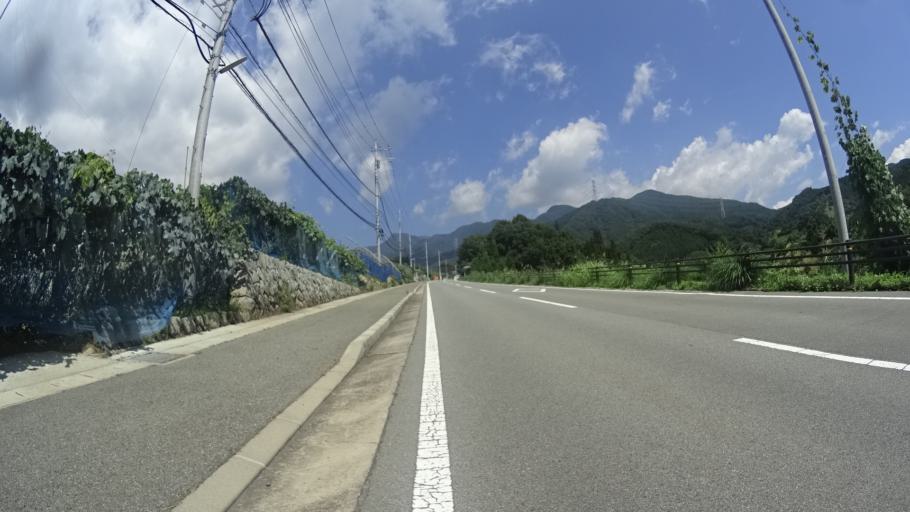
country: JP
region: Yamanashi
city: Enzan
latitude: 35.7610
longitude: 138.7059
